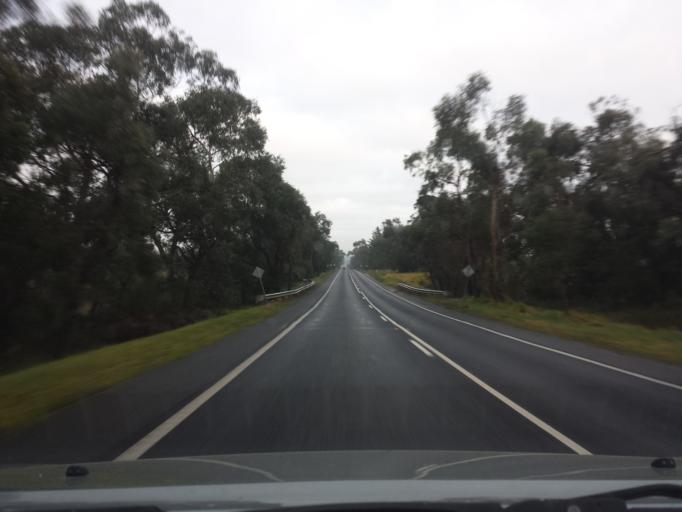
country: AU
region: Victoria
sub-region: Casey
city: Narre Warren North
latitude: -37.9648
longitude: 145.3317
